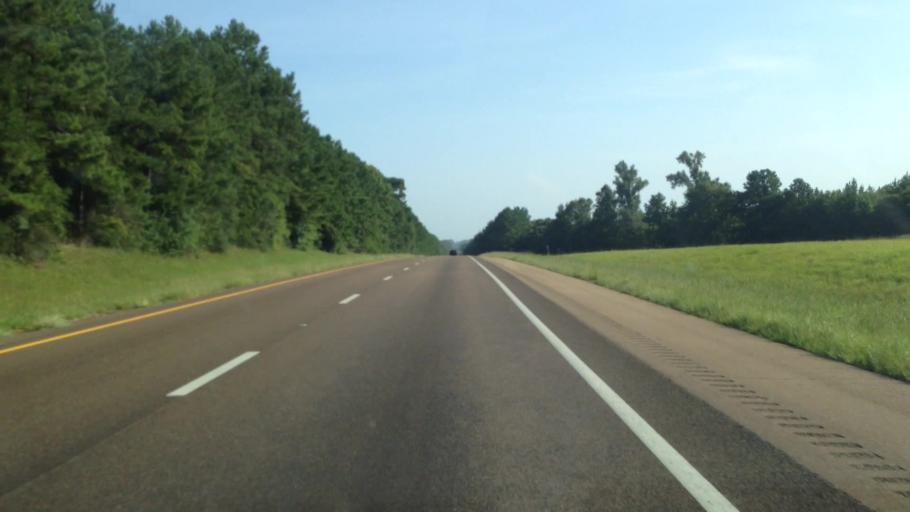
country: US
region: Mississippi
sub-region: Pike County
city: Summit
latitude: 31.3684
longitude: -90.4791
